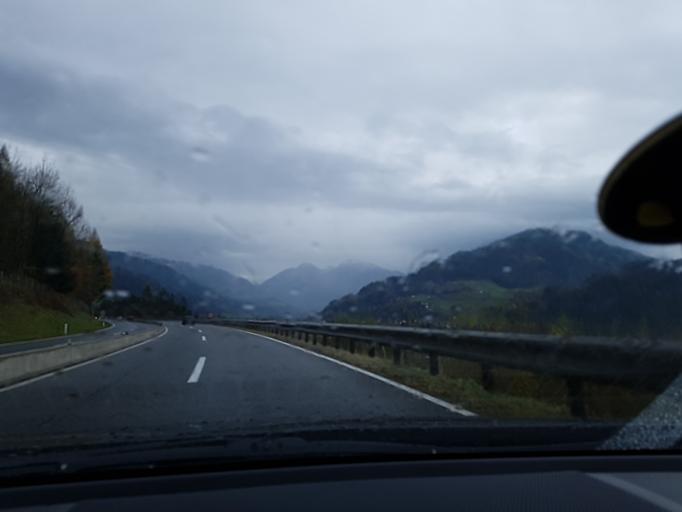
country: AT
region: Salzburg
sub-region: Politischer Bezirk Sankt Johann im Pongau
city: Bischofshofen
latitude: 47.4131
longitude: 13.2231
